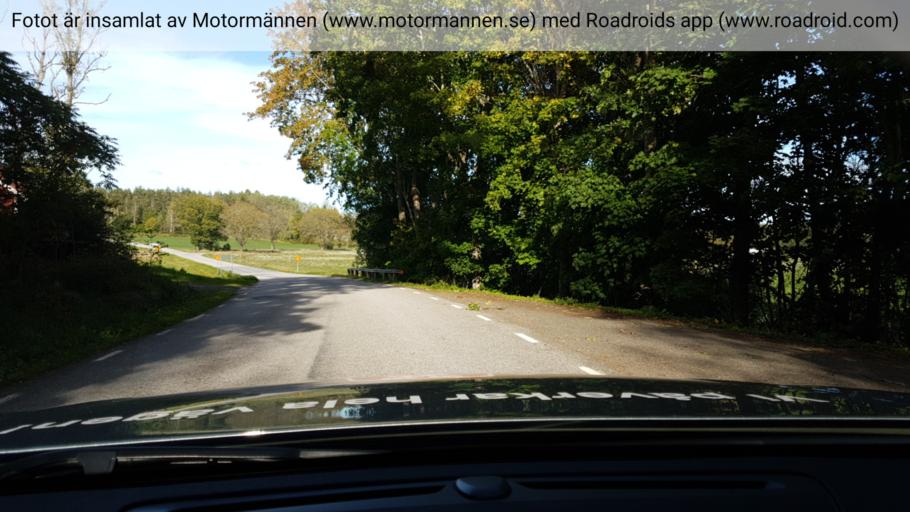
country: SE
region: OEstergoetland
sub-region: Valdemarsviks Kommun
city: Valdemarsvik
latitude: 58.1111
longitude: 16.6513
